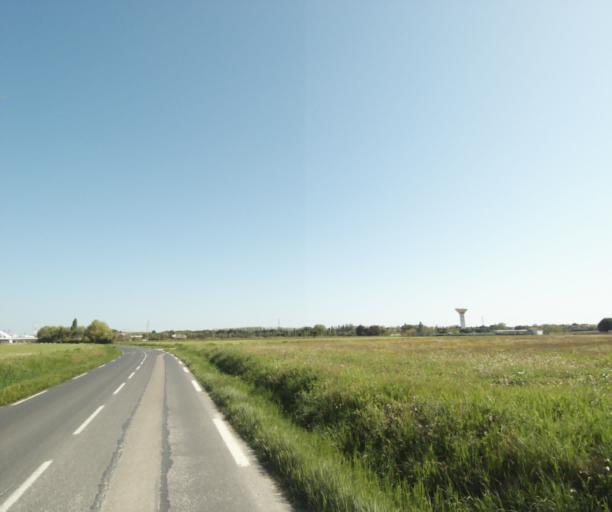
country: FR
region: Languedoc-Roussillon
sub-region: Departement de l'Herault
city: Lattes
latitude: 43.5816
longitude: 3.9087
